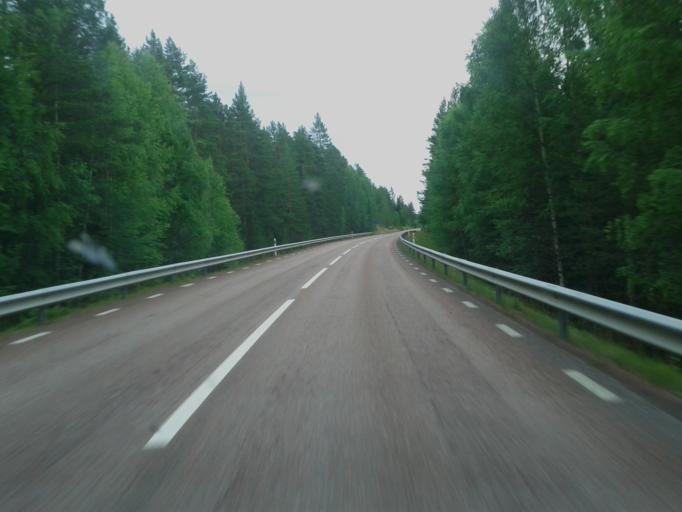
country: SE
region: Dalarna
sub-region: Mora Kommun
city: Mora
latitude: 61.1026
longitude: 14.2922
